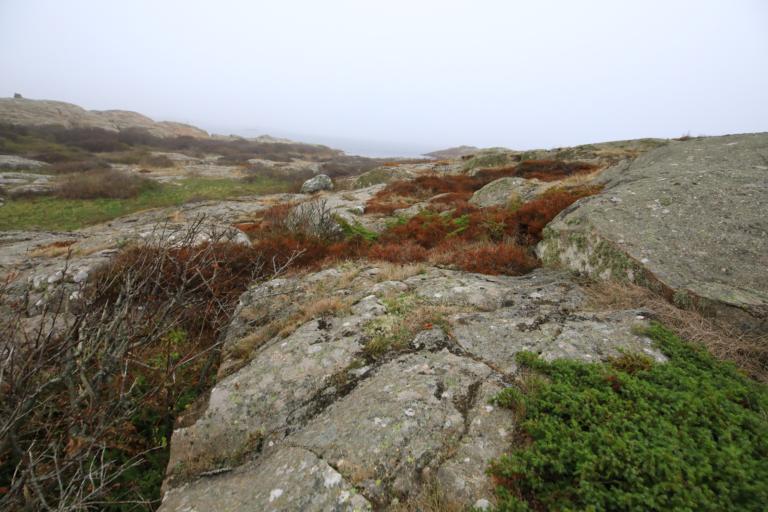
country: SE
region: Vaestra Goetaland
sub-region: Ockero Kommun
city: Hono
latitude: 57.6340
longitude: 11.6059
